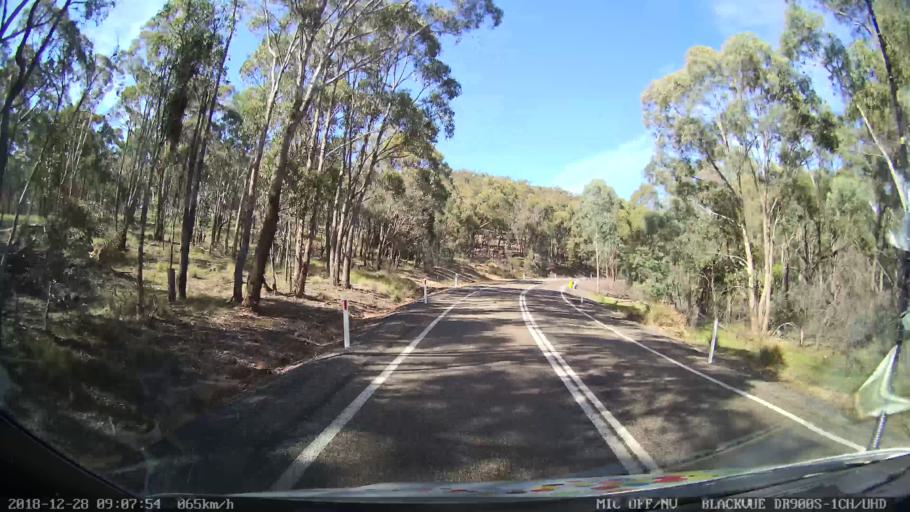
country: AU
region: New South Wales
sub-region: Upper Lachlan Shire
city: Crookwell
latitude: -34.2111
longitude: 149.3436
